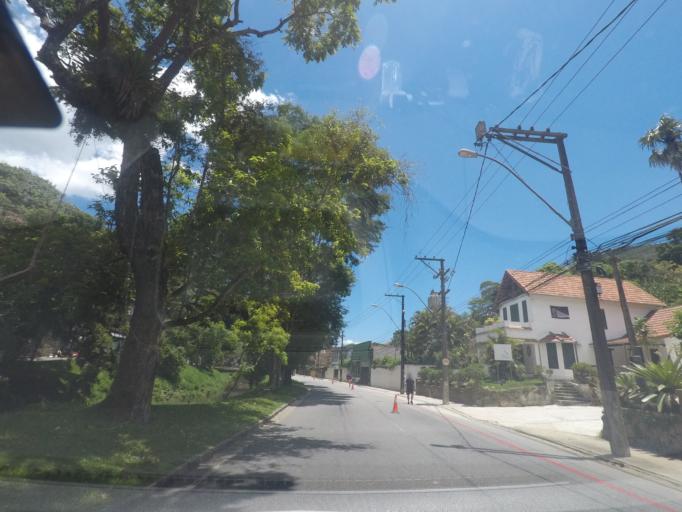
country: BR
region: Rio de Janeiro
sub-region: Petropolis
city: Petropolis
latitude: -22.4951
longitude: -43.1797
